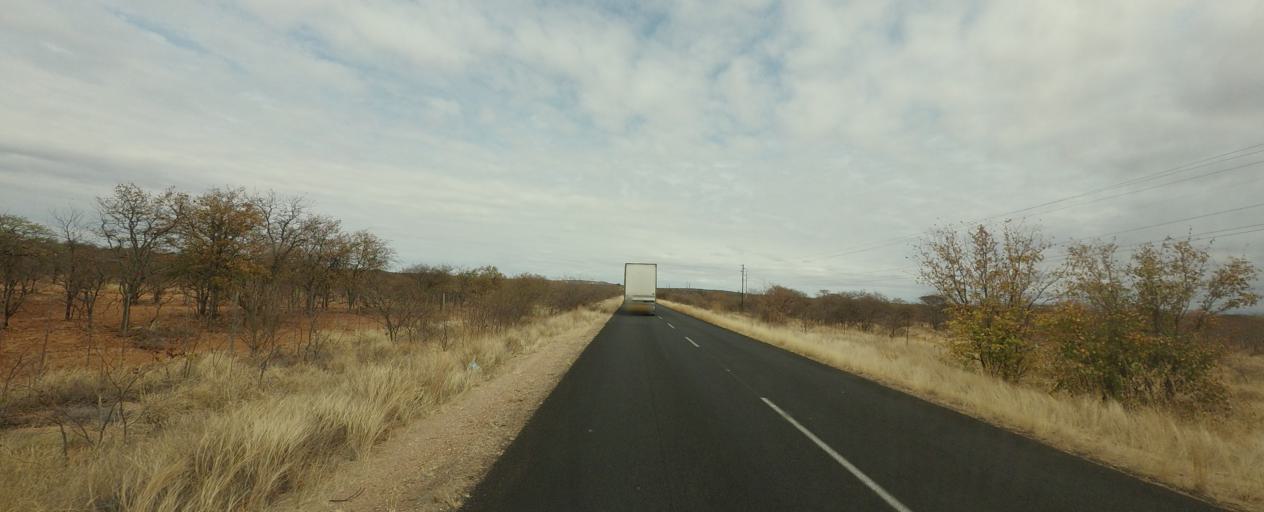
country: ZW
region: Matabeleland South
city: Beitbridge
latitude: -22.4302
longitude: 29.4372
